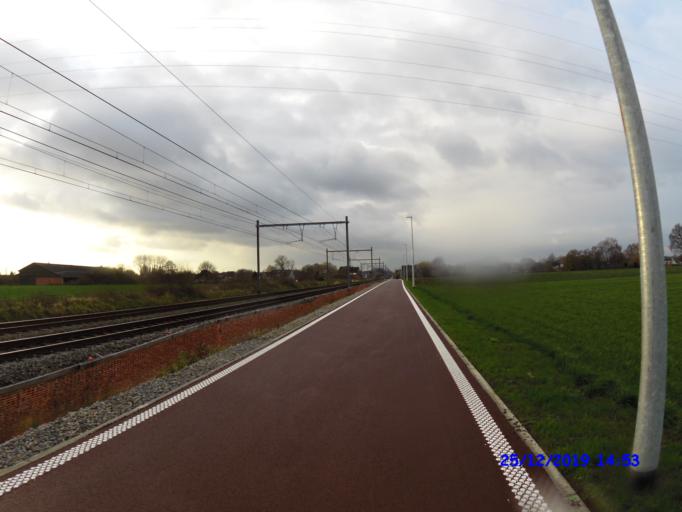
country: BE
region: Flanders
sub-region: Provincie Antwerpen
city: Geel
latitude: 51.1697
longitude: 4.9523
